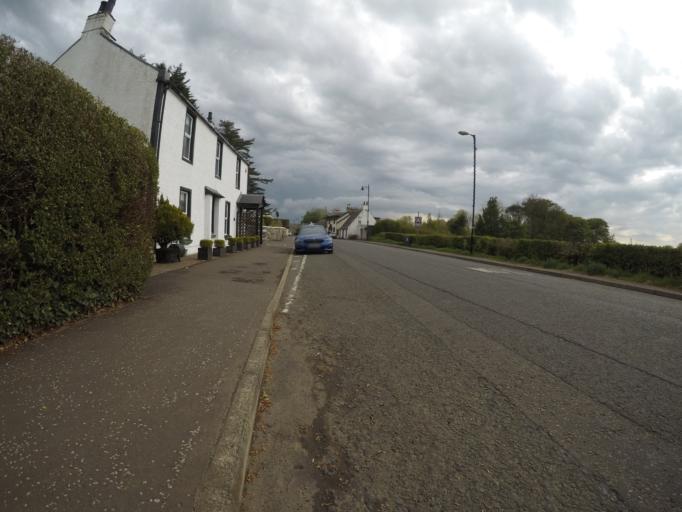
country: GB
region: Scotland
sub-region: East Ayrshire
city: Kilmarnock
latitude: 55.6561
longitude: -4.4455
